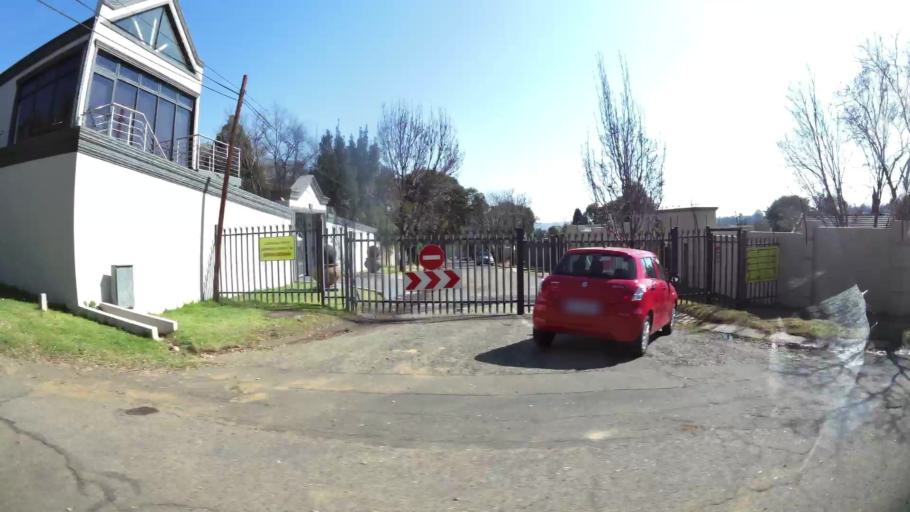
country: ZA
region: Gauteng
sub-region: City of Johannesburg Metropolitan Municipality
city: Johannesburg
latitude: -26.1061
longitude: 28.0441
